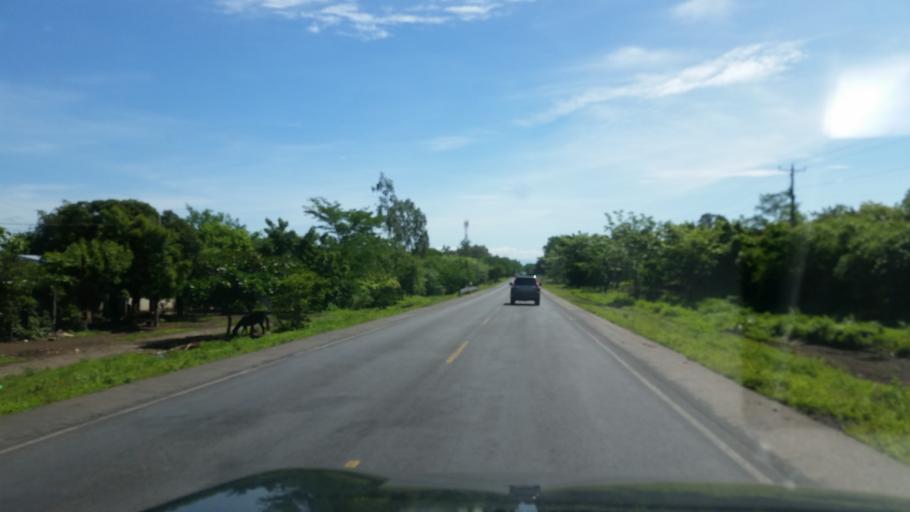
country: NI
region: Chinandega
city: Puerto Morazan
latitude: 12.7619
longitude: -87.0613
